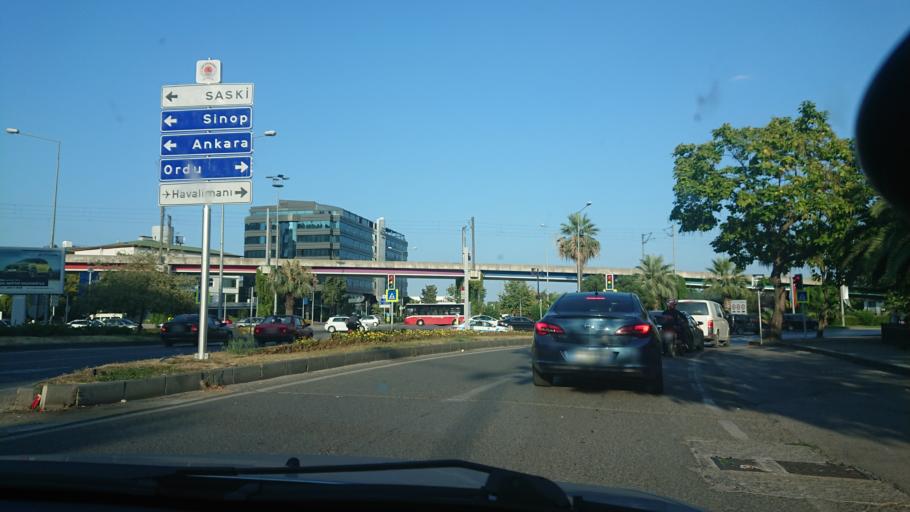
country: TR
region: Samsun
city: Samsun
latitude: 41.3023
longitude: 36.3304
